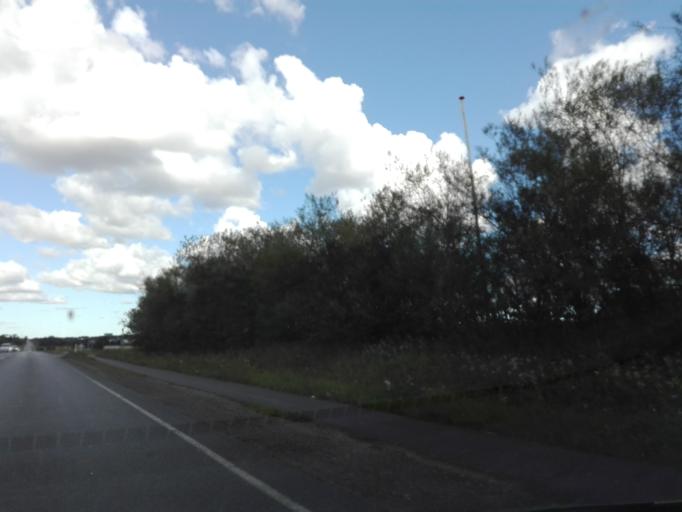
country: DK
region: North Denmark
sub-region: Mariagerfjord Kommune
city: Hobro
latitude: 56.6042
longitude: 9.8066
